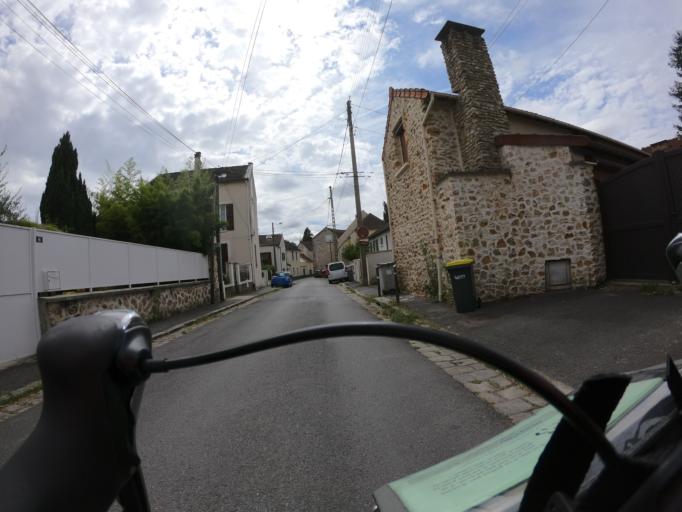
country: FR
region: Ile-de-France
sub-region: Departement de l'Essonne
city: Igny
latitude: 48.7450
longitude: 2.2263
